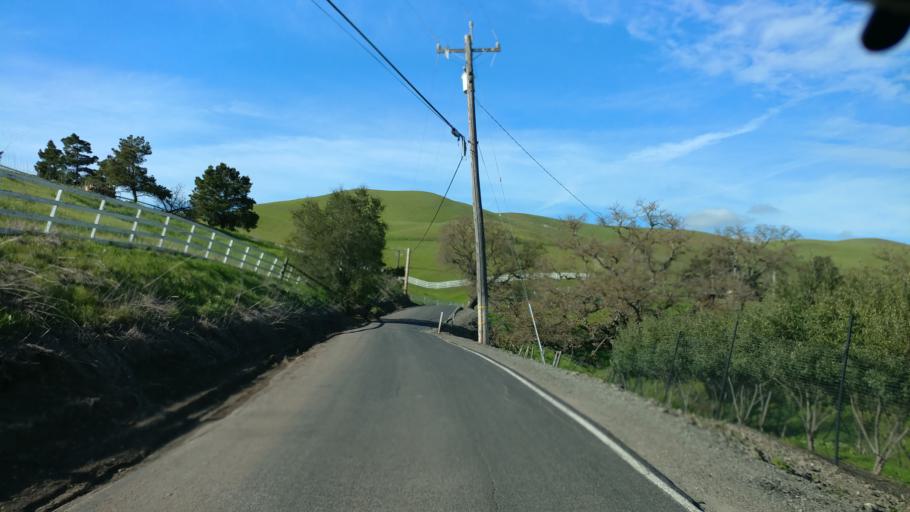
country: US
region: California
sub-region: Alameda County
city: Livermore
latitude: 37.7740
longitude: -121.7787
